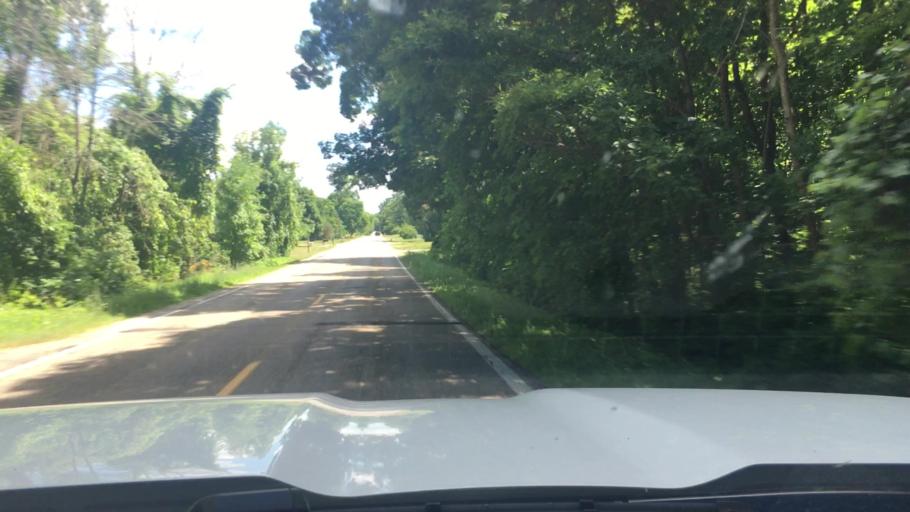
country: US
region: Michigan
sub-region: Kent County
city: Sparta
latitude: 43.1466
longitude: -85.6409
